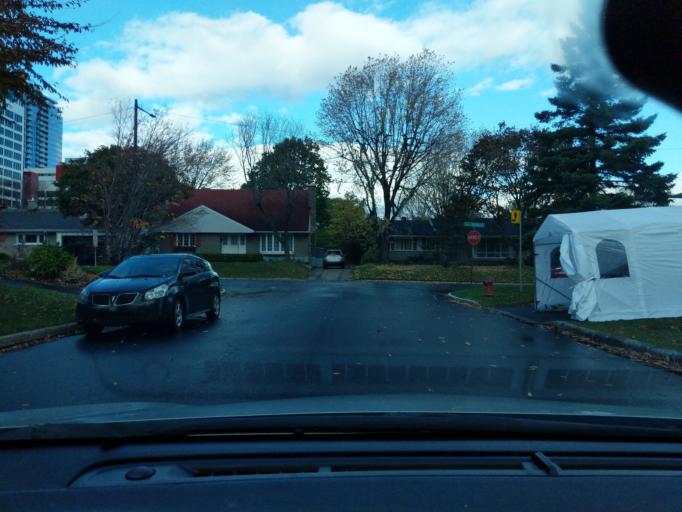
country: CA
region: Quebec
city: L'Ancienne-Lorette
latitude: 46.7642
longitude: -71.2900
